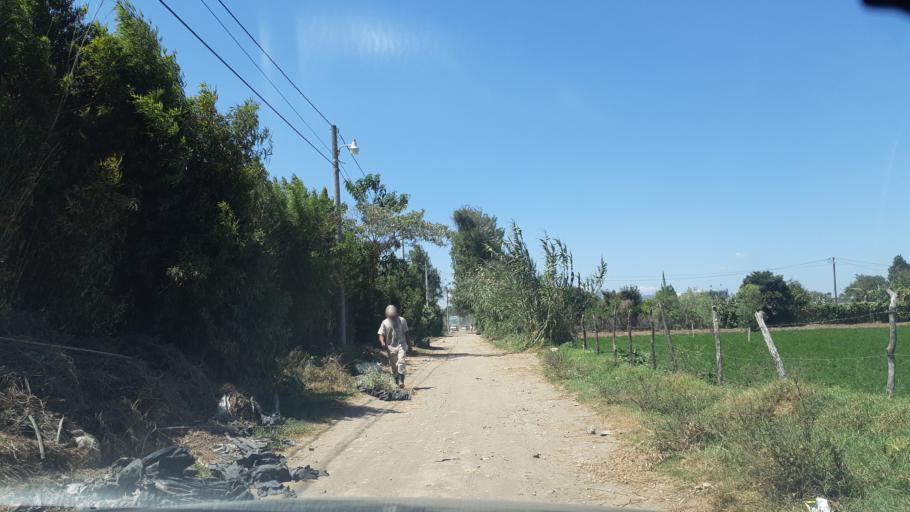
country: GT
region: Chimaltenango
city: El Tejar
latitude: 14.6455
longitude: -90.8085
